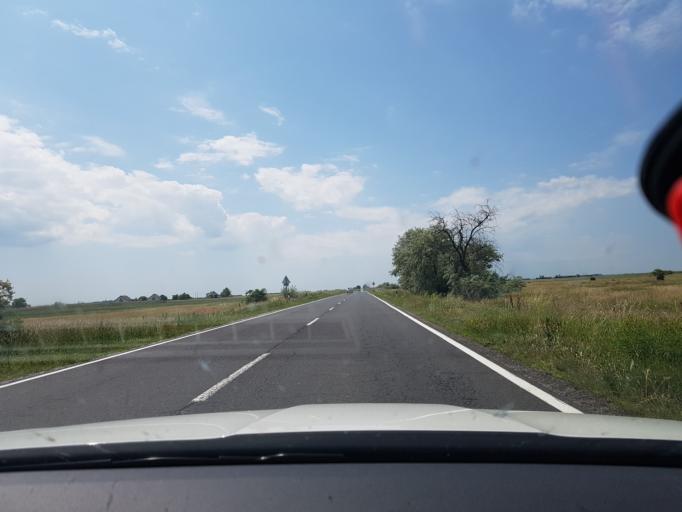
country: HU
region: Hajdu-Bihar
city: Egyek
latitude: 47.5708
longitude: 20.9875
